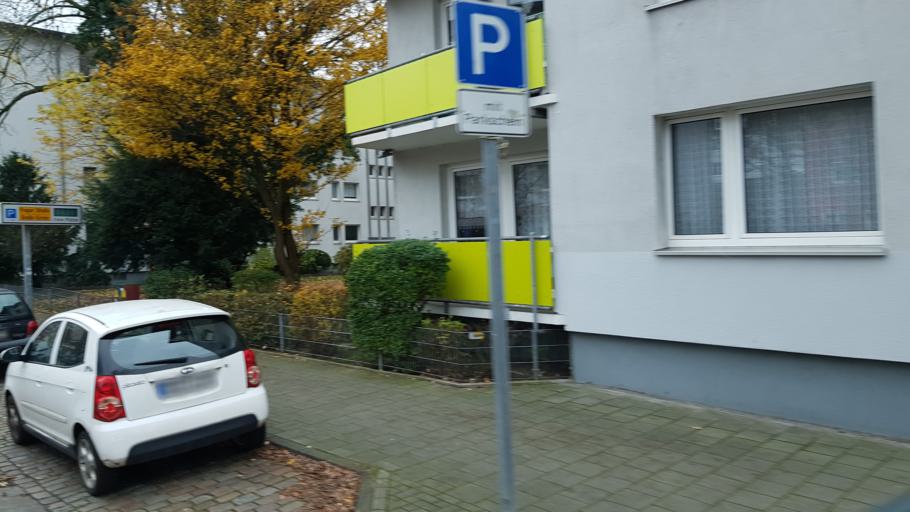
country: DE
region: Bremen
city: Bremerhaven
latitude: 53.5461
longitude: 8.5786
